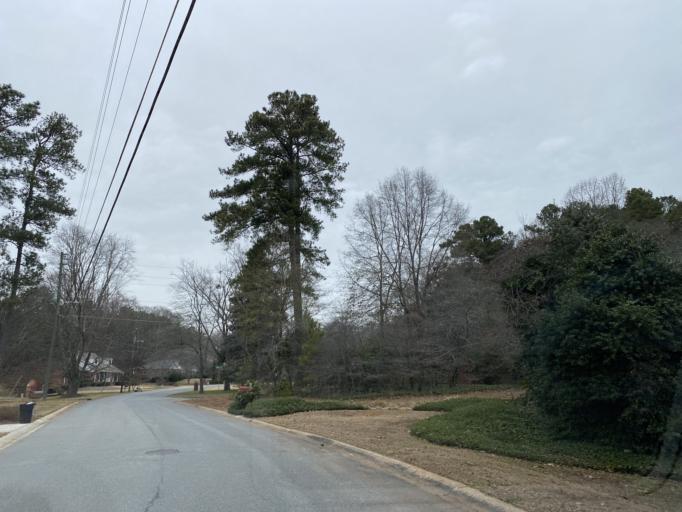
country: US
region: Georgia
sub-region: Cobb County
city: Fair Oaks
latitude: 33.9202
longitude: -84.5697
